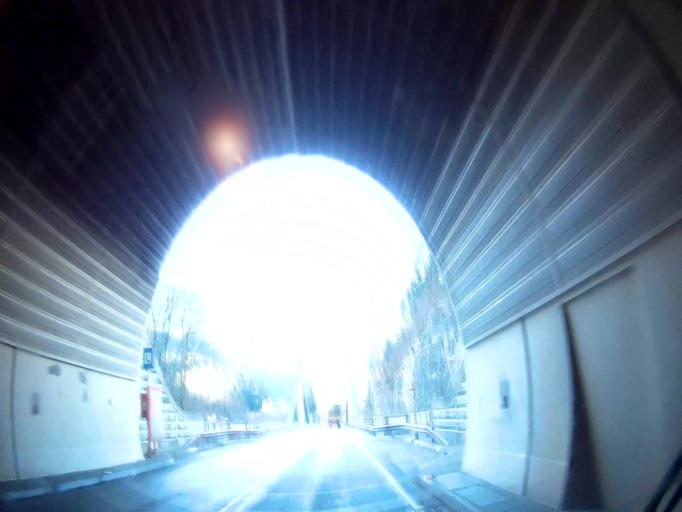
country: AT
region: Salzburg
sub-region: Politischer Bezirk Zell am See
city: Unken
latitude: 47.6501
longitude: 12.7370
